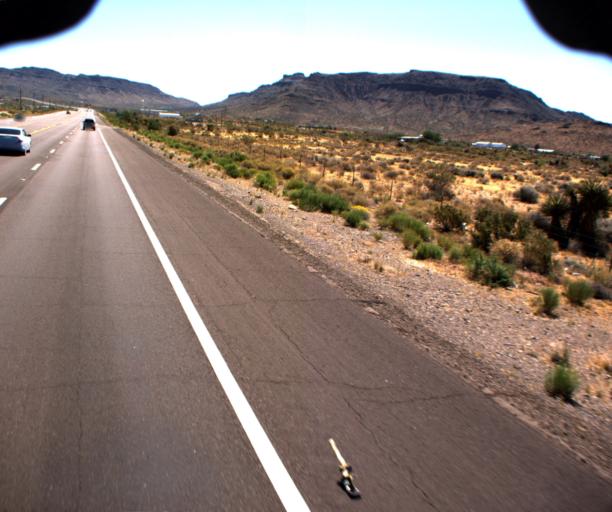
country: US
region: Arizona
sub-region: Mohave County
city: Golden Valley
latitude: 35.2190
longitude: -114.1557
